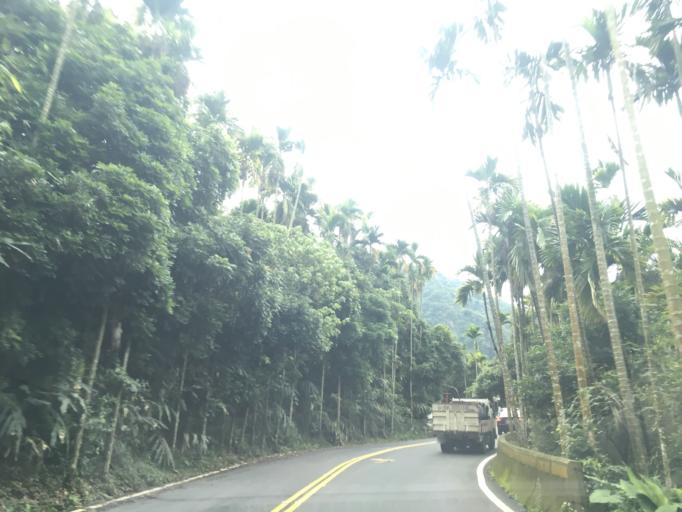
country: TW
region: Taiwan
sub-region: Chiayi
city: Jiayi Shi
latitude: 23.5575
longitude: 120.5855
